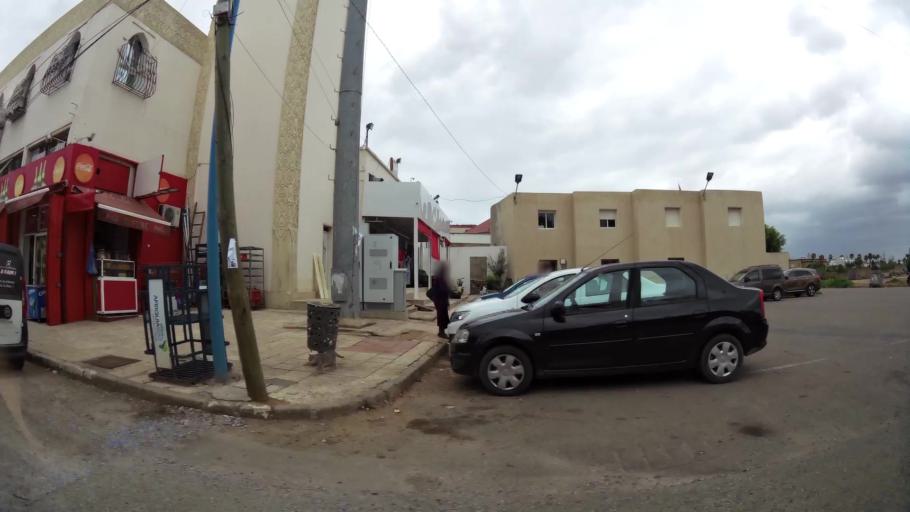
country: MA
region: Grand Casablanca
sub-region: Casablanca
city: Casablanca
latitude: 33.5419
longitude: -7.6339
